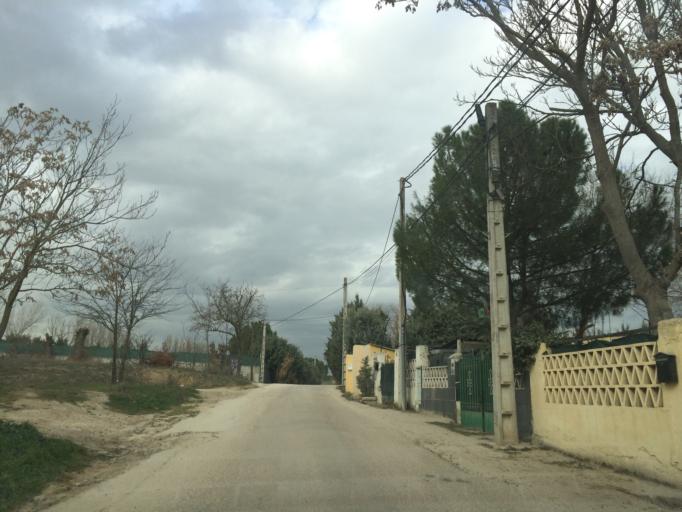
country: ES
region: Madrid
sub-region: Provincia de Madrid
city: Arroyomolinos
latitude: 40.3110
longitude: -3.9467
